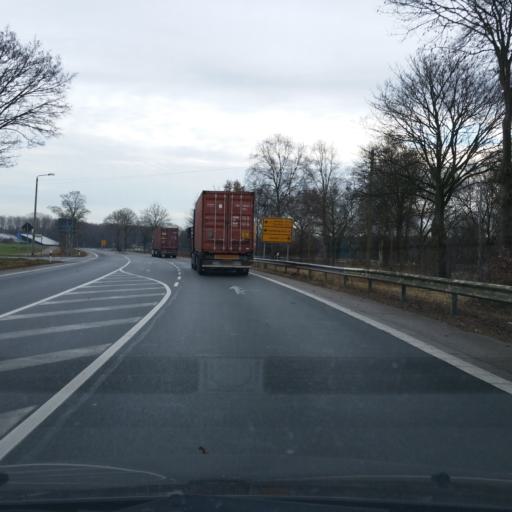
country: DE
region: North Rhine-Westphalia
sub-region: Regierungsbezirk Munster
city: Isselburg
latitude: 51.8157
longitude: 6.4720
